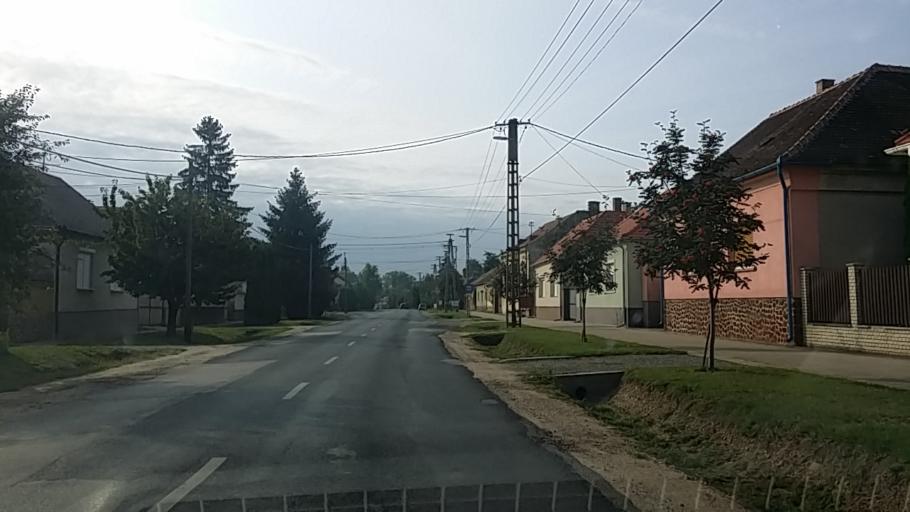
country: HU
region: Gyor-Moson-Sopron
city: Fertoszentmiklos
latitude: 47.6062
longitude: 16.9063
